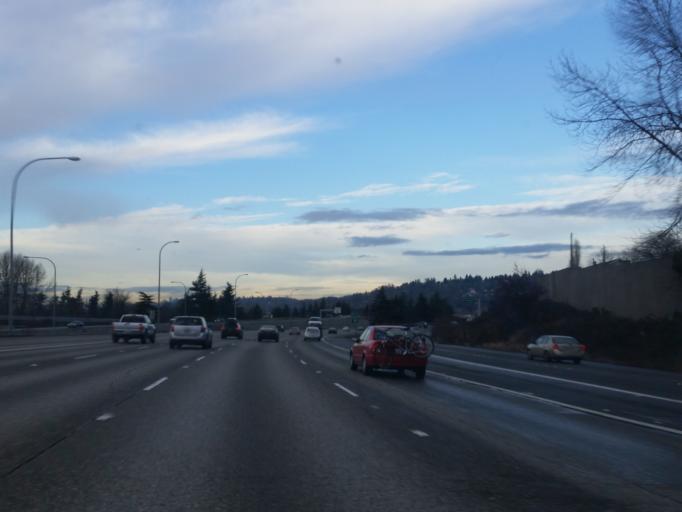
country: US
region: Washington
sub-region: King County
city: Tukwila
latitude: 47.4783
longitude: -122.2714
